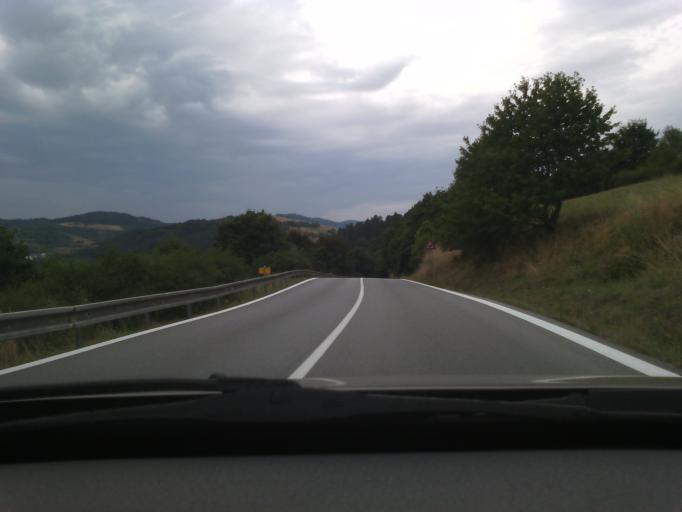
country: SK
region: Presovsky
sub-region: Okres Stara Lubovna
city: Vysne Ruzbachy
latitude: 49.2841
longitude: 20.6018
